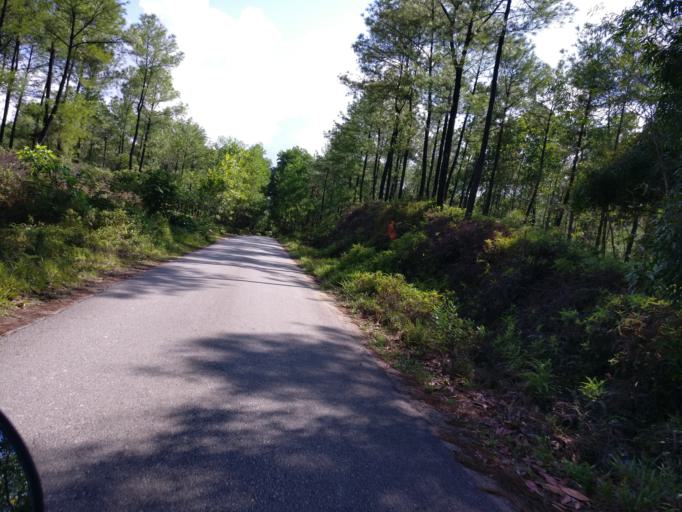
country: VN
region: Thua Thien-Hue
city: Hue
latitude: 16.4079
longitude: 107.5934
